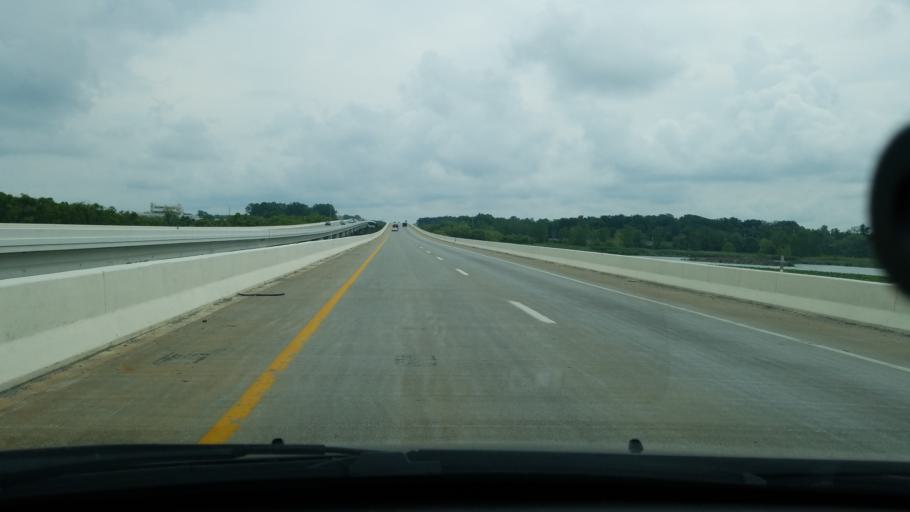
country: US
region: Ohio
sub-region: Erie County
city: Huron
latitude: 41.3698
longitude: -82.5530
